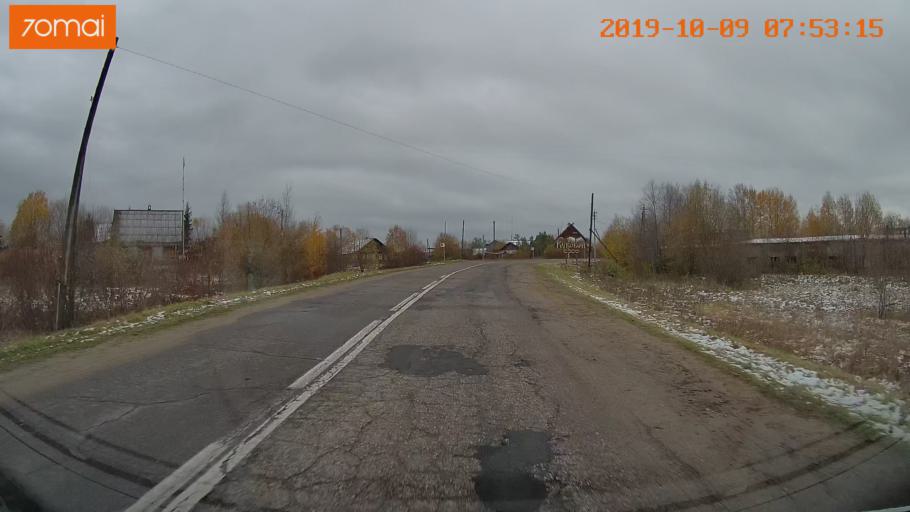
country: RU
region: Jaroslavl
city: Kukoboy
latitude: 58.6973
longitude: 39.8935
